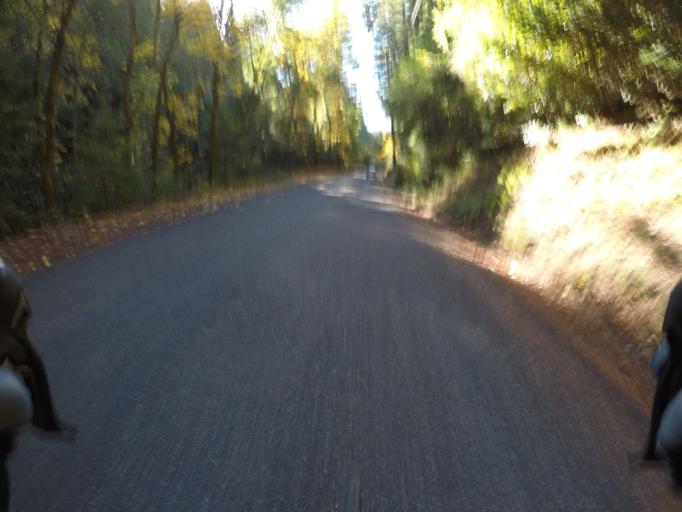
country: US
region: California
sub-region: Santa Cruz County
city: Lompico
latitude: 37.1024
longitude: -122.0314
